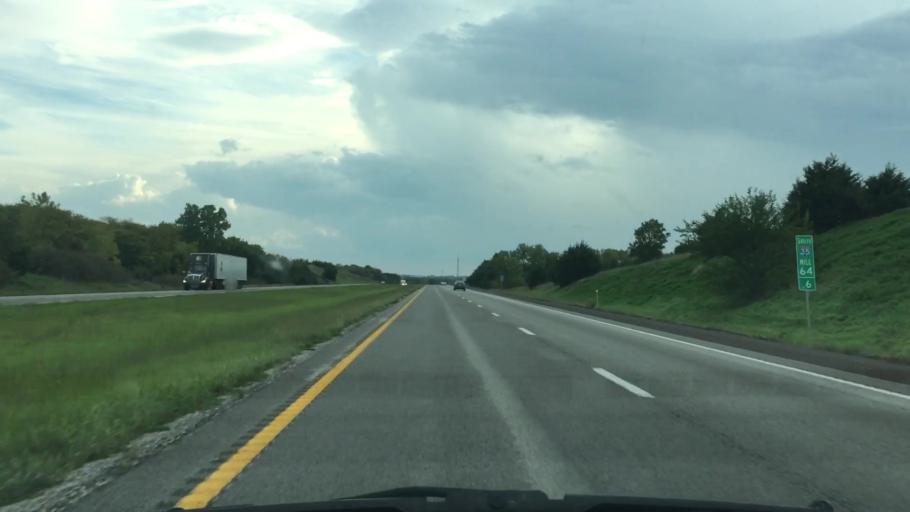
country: US
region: Missouri
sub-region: Clinton County
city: Cameron
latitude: 39.8951
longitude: -94.1540
